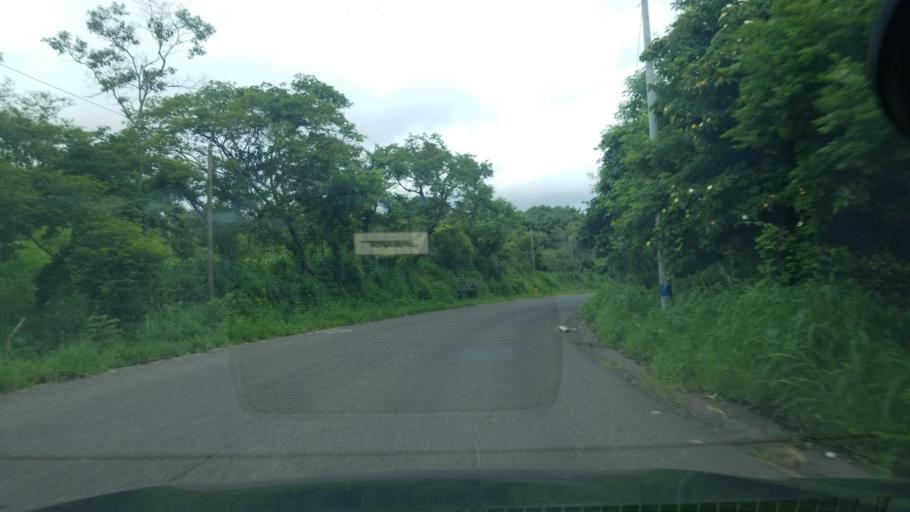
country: HN
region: Choluteca
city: San Marcos de Colon
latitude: 13.4267
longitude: -86.8292
